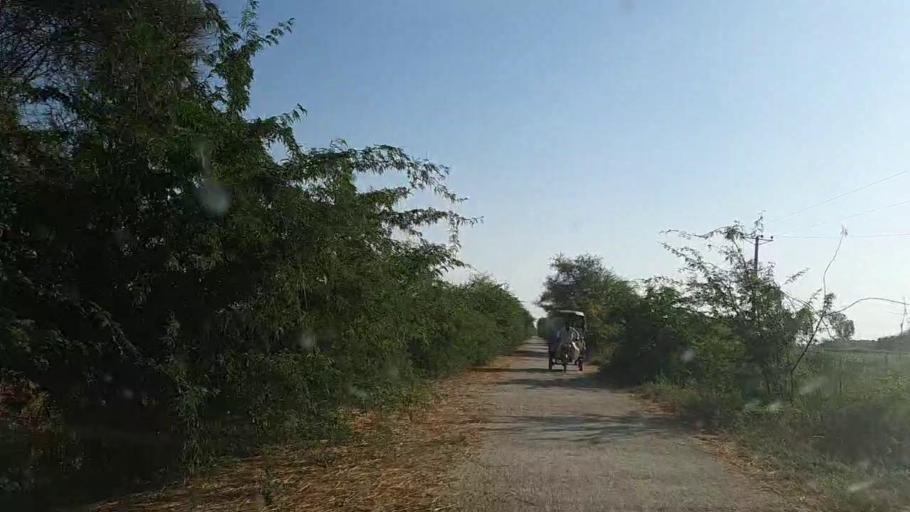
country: PK
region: Sindh
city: Daro Mehar
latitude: 24.6498
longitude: 68.0750
